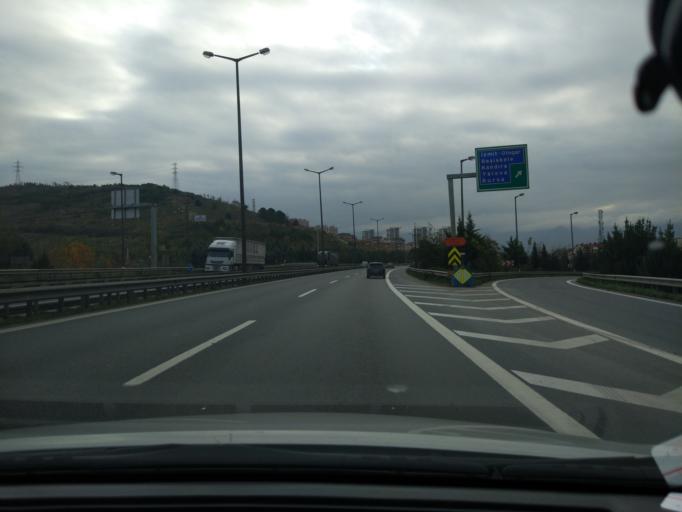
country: TR
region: Kocaeli
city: Kullar
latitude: 40.7823
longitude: 29.9763
